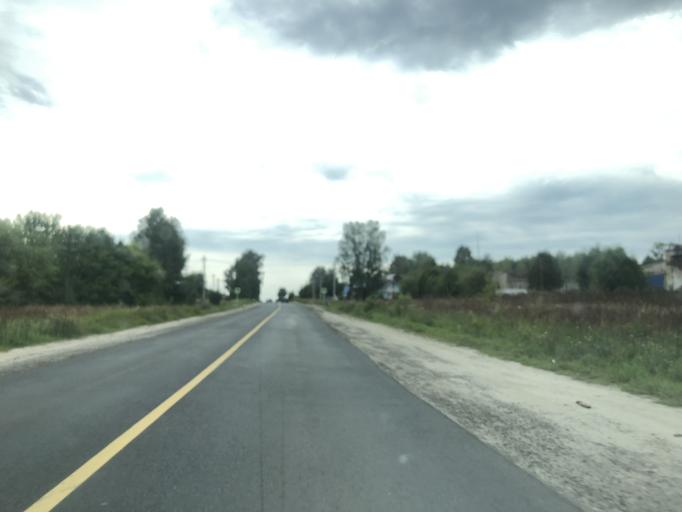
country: RU
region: Ivanovo
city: Pestyaki
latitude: 56.7054
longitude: 42.6919
